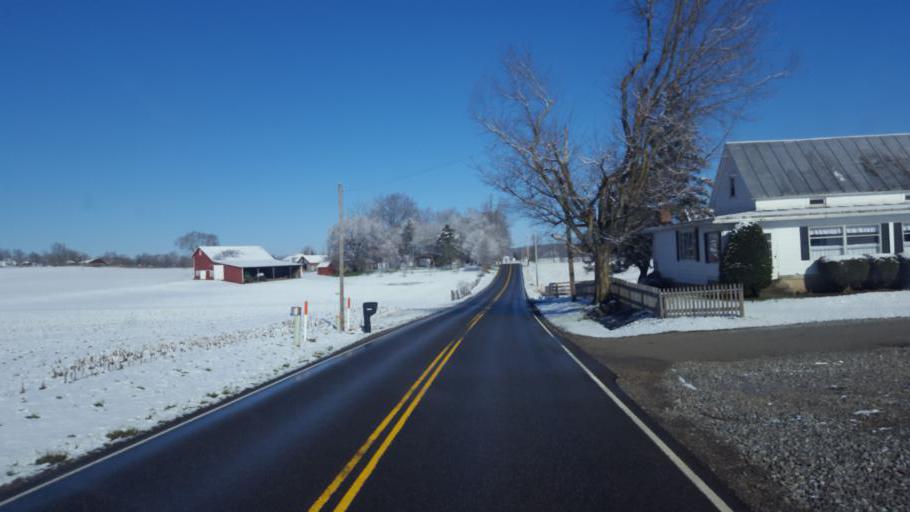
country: US
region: Ohio
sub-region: Knox County
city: Fredericktown
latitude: 40.5324
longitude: -82.6036
